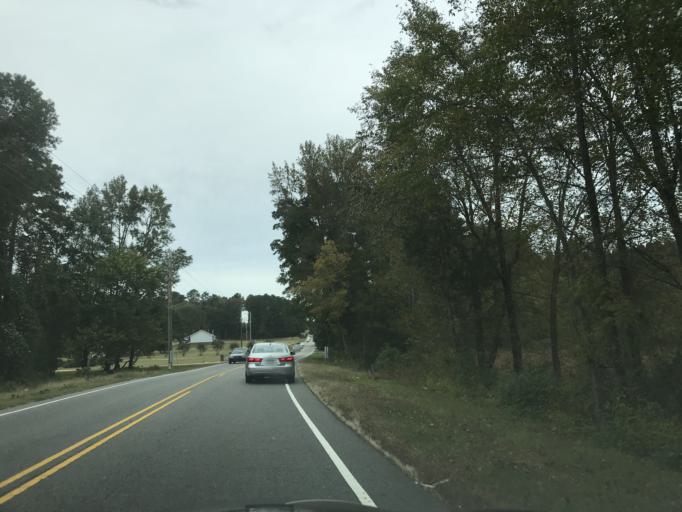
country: US
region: North Carolina
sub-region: Wake County
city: Rolesville
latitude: 35.9153
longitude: -78.5063
